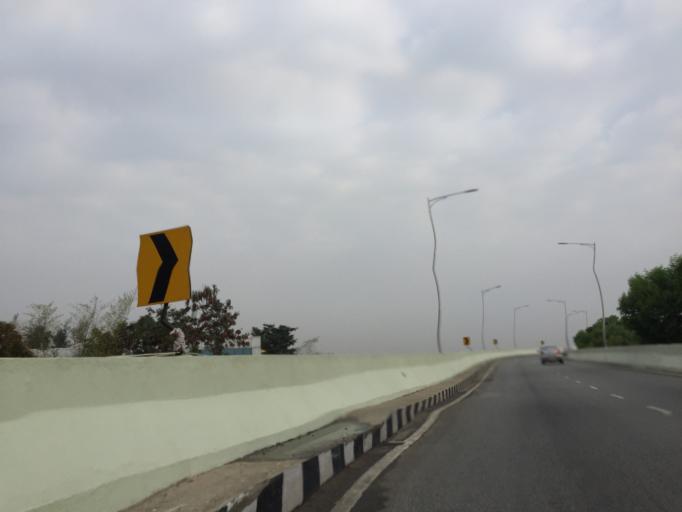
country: IN
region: Karnataka
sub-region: Bangalore Rural
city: Devanhalli
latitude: 13.2009
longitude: 77.6582
